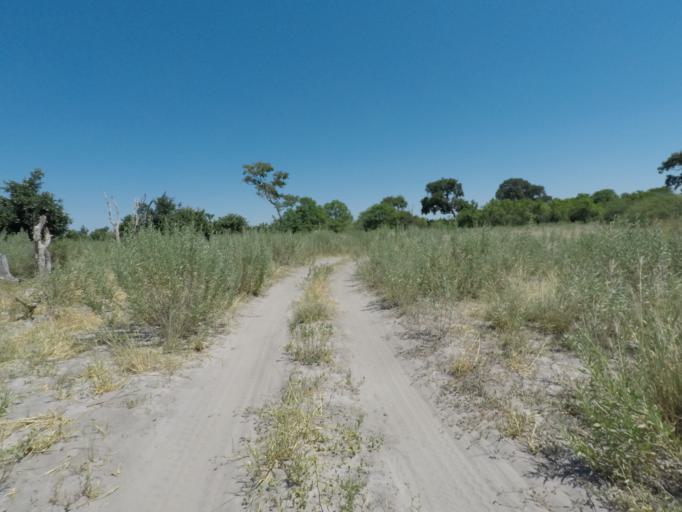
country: BW
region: North West
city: Maun
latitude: -19.4733
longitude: 23.5543
